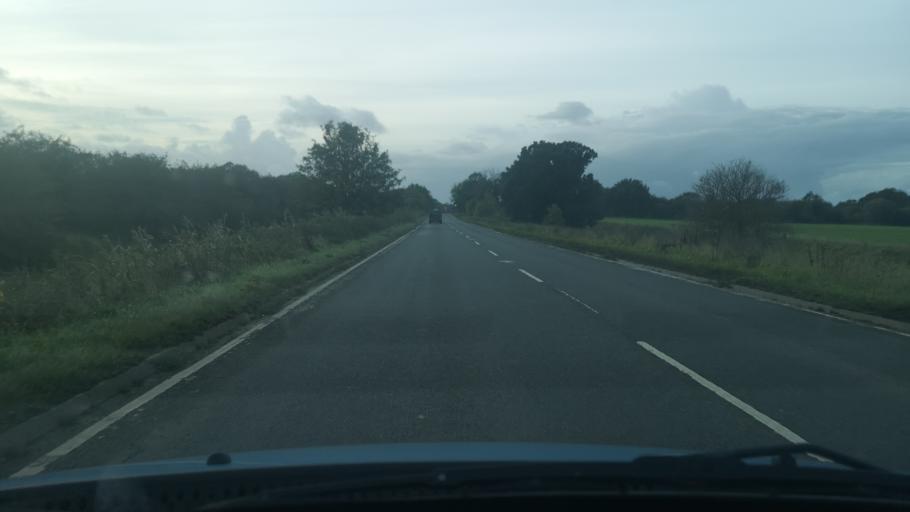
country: GB
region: England
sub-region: North Lincolnshire
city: Belton
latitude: 53.5823
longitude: -0.8035
